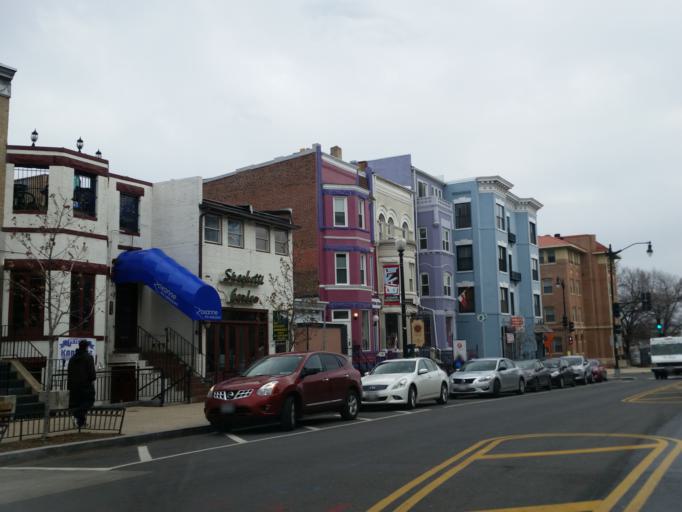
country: US
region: Washington, D.C.
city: Washington, D.C.
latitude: 38.9203
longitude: -77.0419
